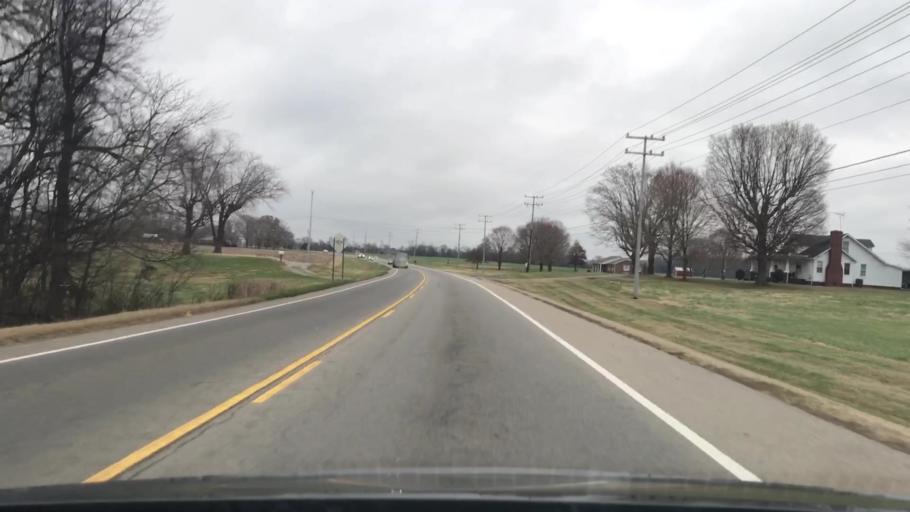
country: US
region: Kentucky
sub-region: Todd County
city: Guthrie
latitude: 36.6109
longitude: -87.2512
